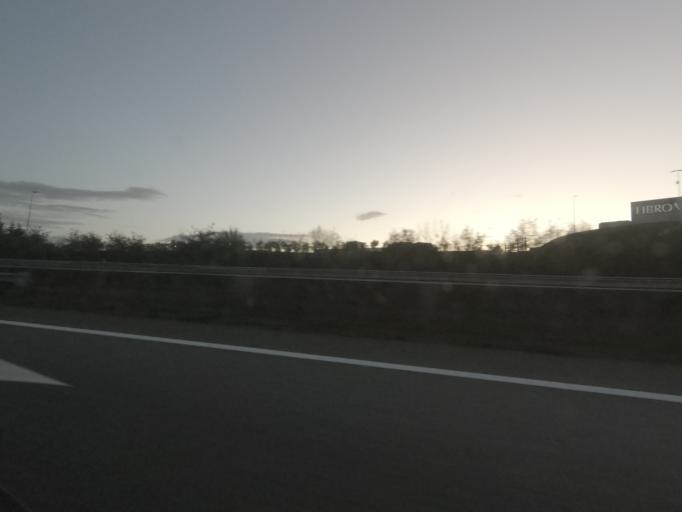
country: PT
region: Porto
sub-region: Valongo
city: Campo
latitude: 41.1765
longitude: -8.4412
